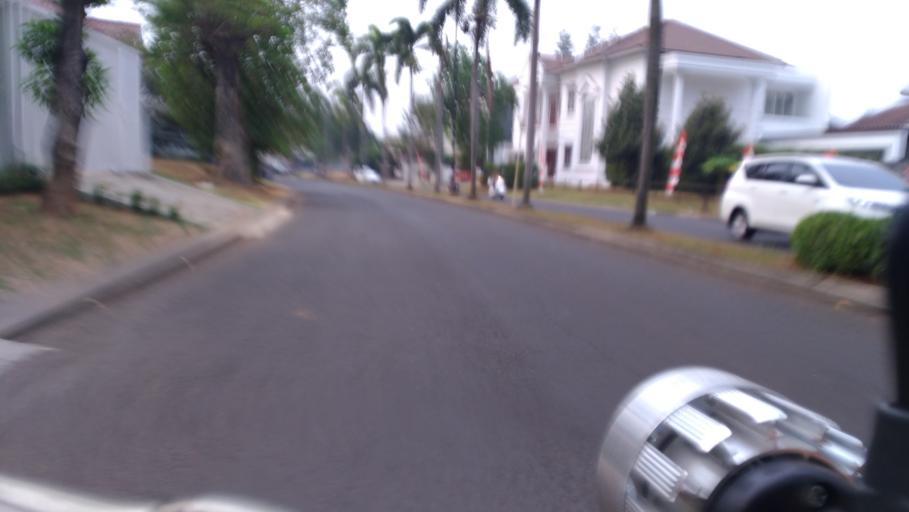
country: ID
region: West Java
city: Cileungsir
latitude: -6.4026
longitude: 106.9425
